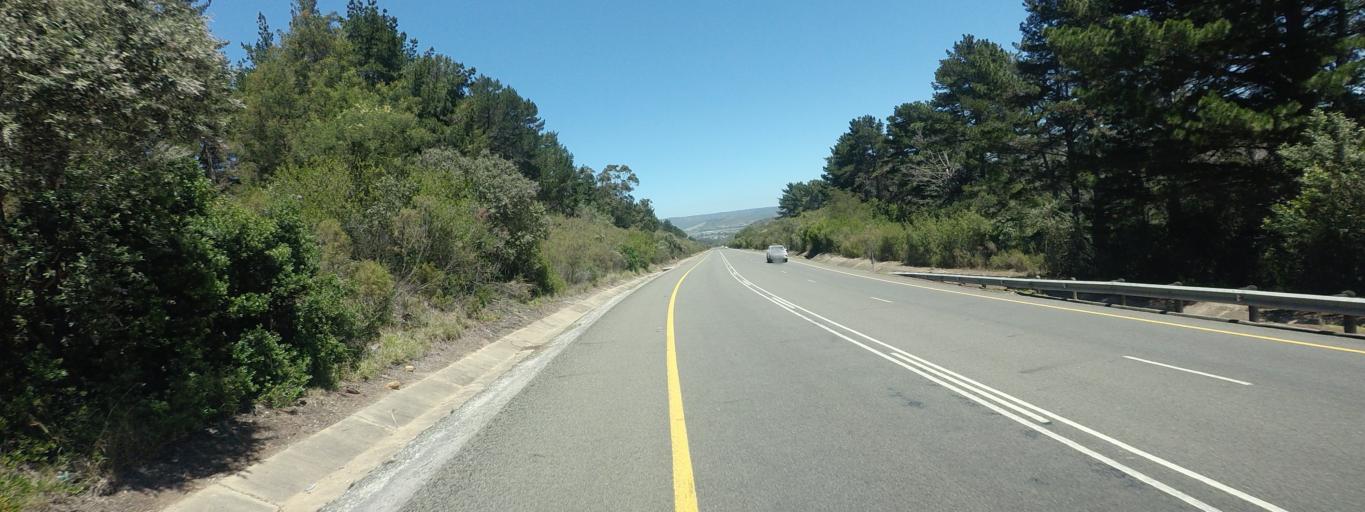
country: ZA
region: Western Cape
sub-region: Eden District Municipality
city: Plettenberg Bay
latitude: -34.0002
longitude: 23.4318
